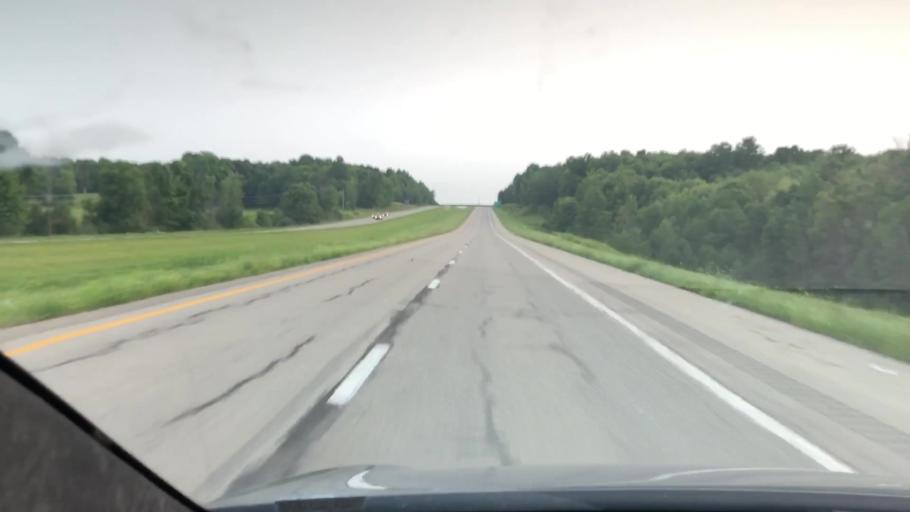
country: US
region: Pennsylvania
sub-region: Venango County
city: Sugarcreek
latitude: 41.2569
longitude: -79.9340
